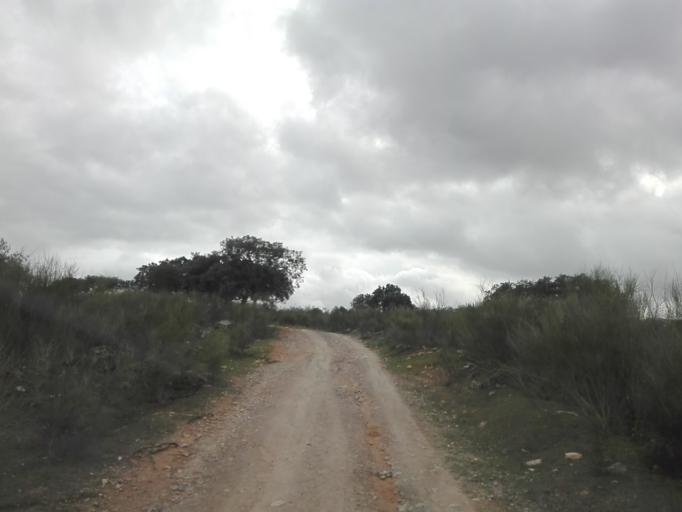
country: ES
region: Extremadura
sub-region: Provincia de Badajoz
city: Hinojosa del Valle
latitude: 38.4380
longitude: -6.1933
